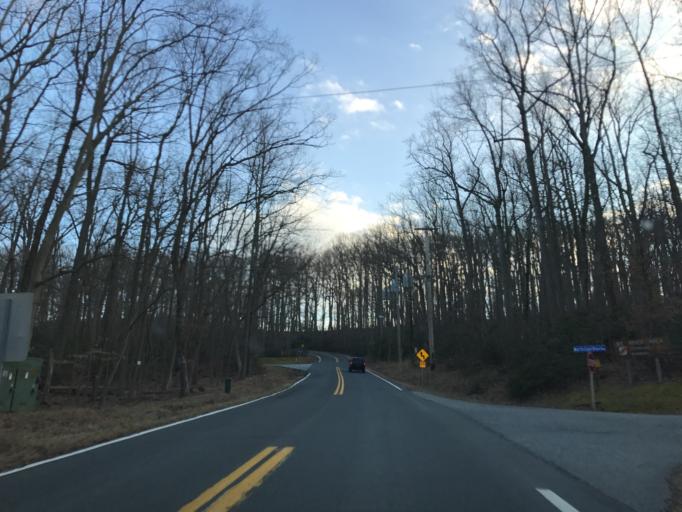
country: US
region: Maryland
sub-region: Cecil County
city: Charlestown
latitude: 39.4813
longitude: -75.9850
